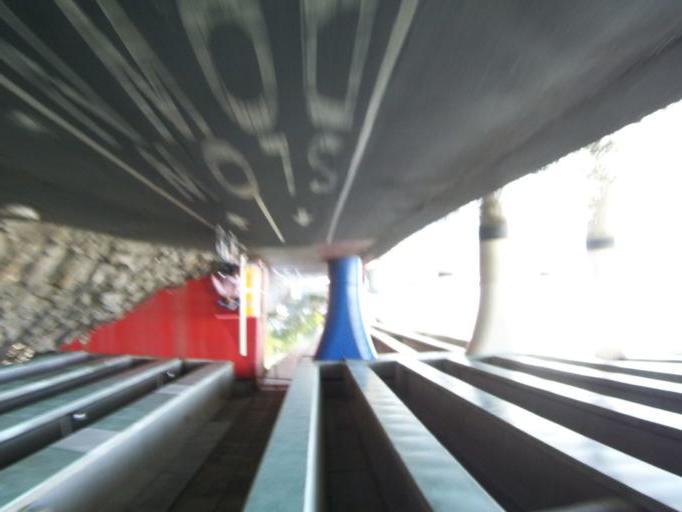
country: AU
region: Queensland
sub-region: Brisbane
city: Brisbane
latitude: -27.4708
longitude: 153.0213
